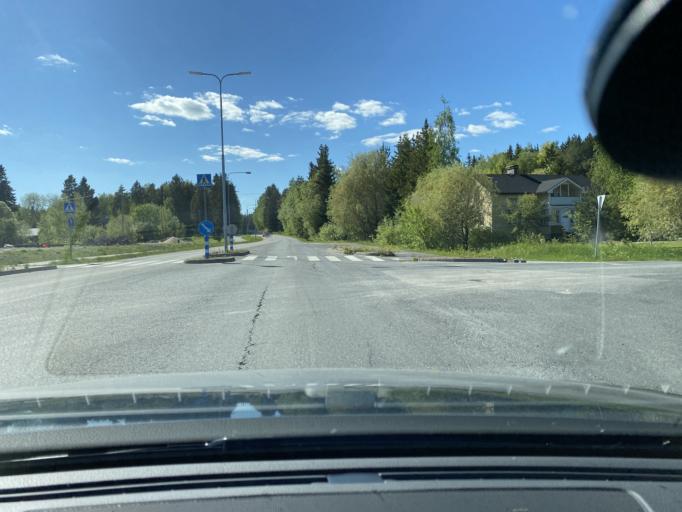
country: FI
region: Varsinais-Suomi
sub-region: Turku
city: Kaarina
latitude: 60.4178
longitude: 22.3425
